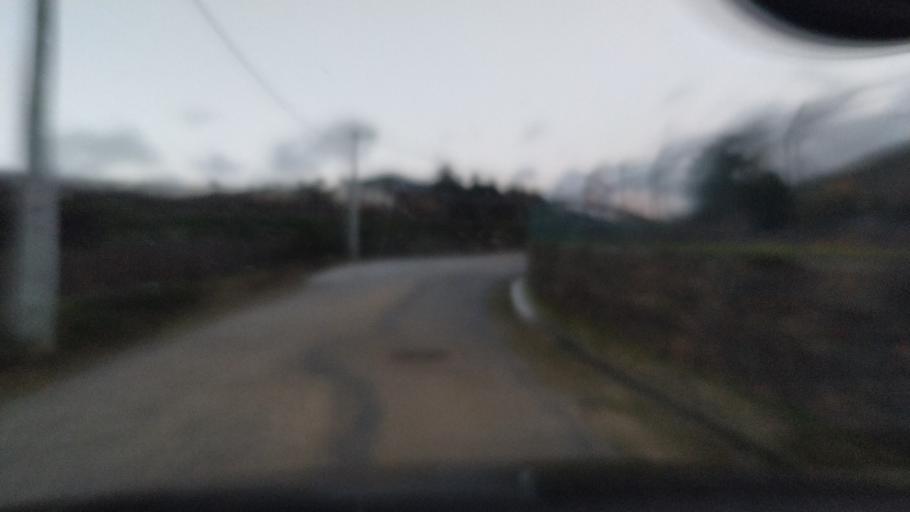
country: PT
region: Vila Real
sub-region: Santa Marta de Penaguiao
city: Santa Marta de Penaguiao
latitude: 41.2332
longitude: -7.7794
